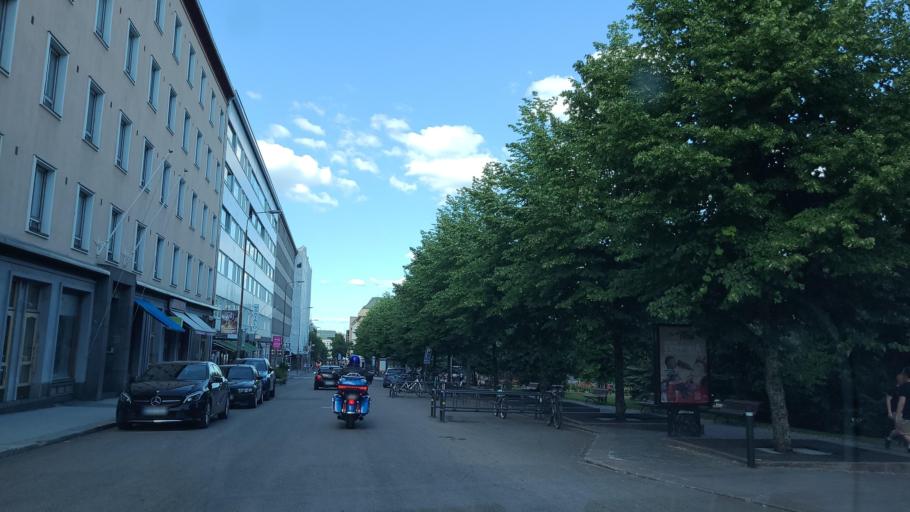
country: FI
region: Central Finland
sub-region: Jyvaeskylae
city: Jyvaeskylae
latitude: 62.2403
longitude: 25.7427
